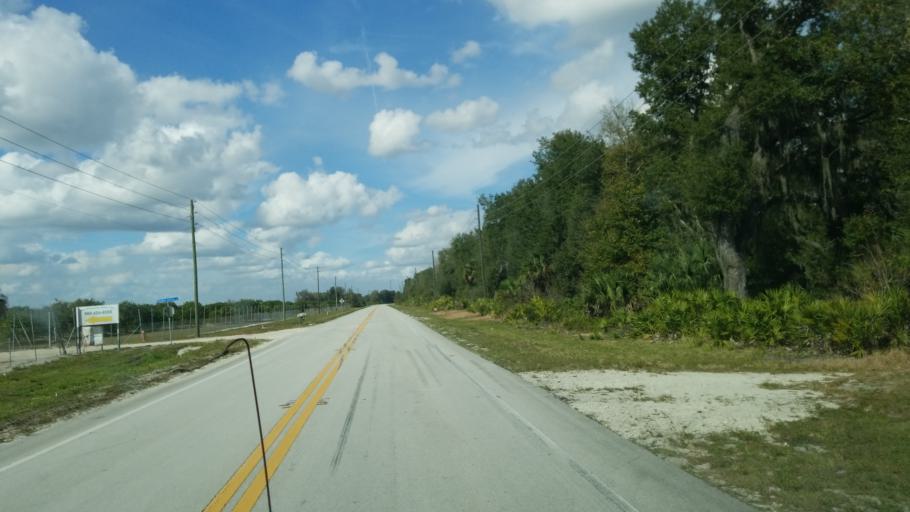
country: US
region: Florida
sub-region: Osceola County
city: Saint Cloud
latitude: 28.0933
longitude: -81.0748
